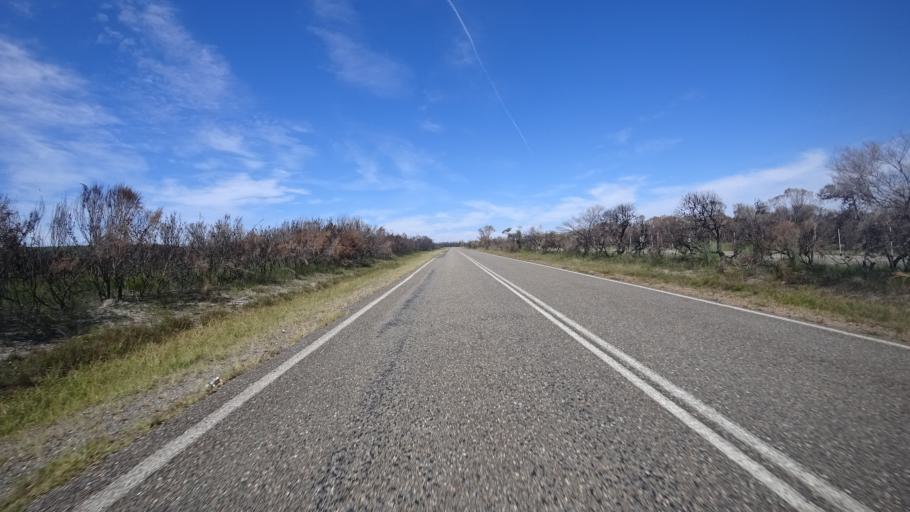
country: AU
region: New South Wales
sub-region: Shoalhaven Shire
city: Falls Creek
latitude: -35.1487
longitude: 150.7079
